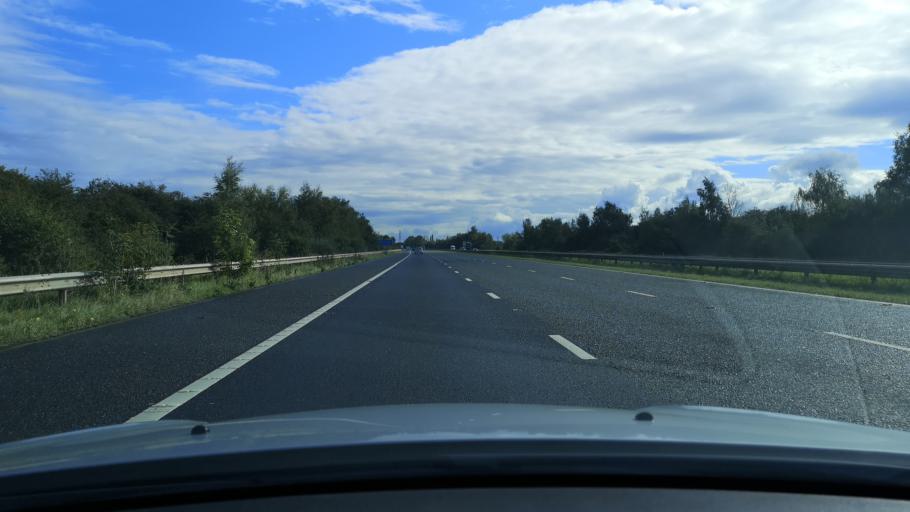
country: GB
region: England
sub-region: East Riding of Yorkshire
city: Pollington
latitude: 53.6850
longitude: -1.0846
